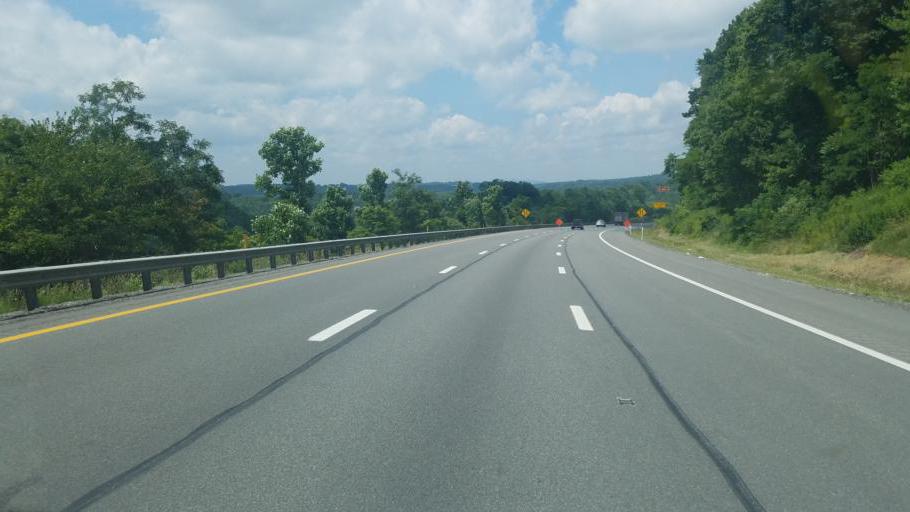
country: US
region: West Virginia
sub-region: Raleigh County
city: MacArthur
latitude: 37.7335
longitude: -81.2037
